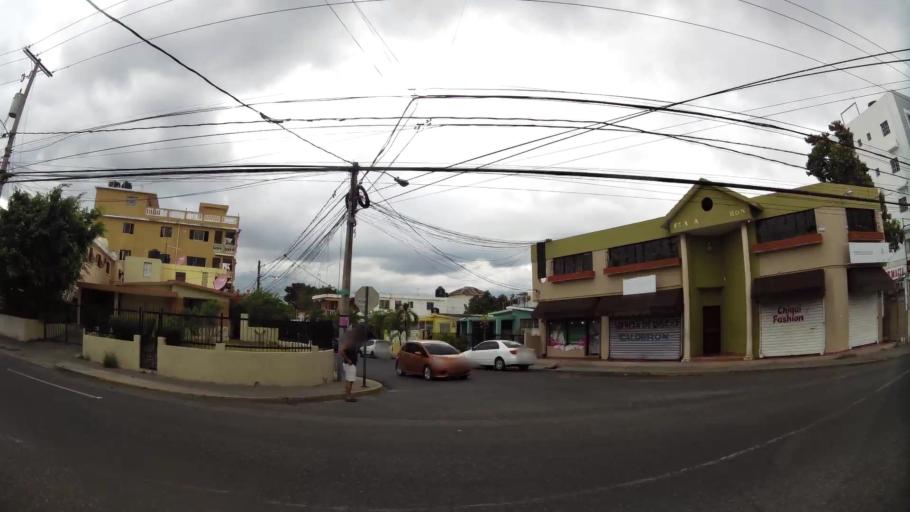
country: DO
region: Nacional
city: La Agustina
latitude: 18.4942
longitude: -69.9300
